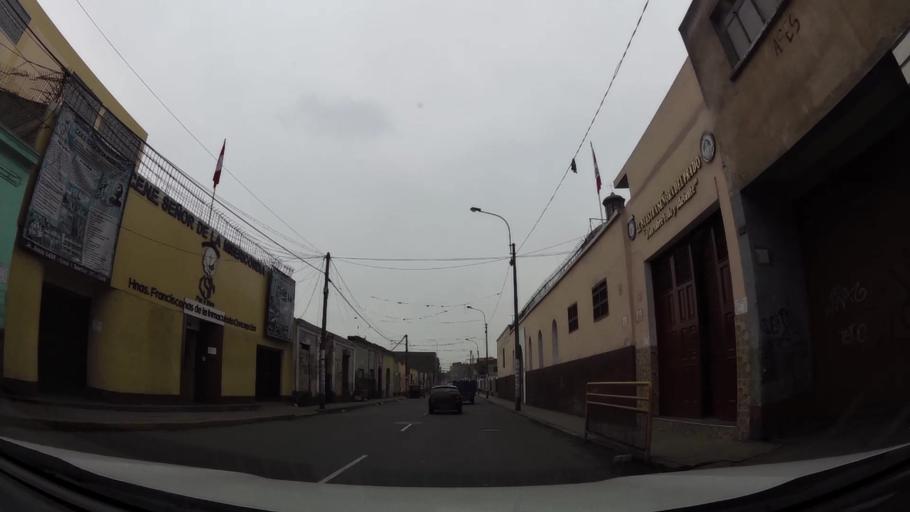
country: PE
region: Lima
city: Lima
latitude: -12.0519
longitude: -77.0150
